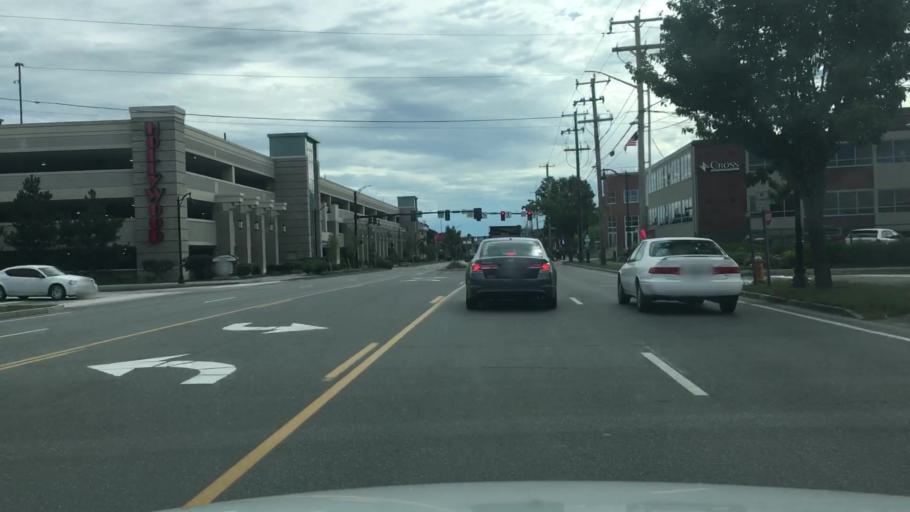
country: US
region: Maine
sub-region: Penobscot County
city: Bangor
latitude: 44.7904
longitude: -68.7771
